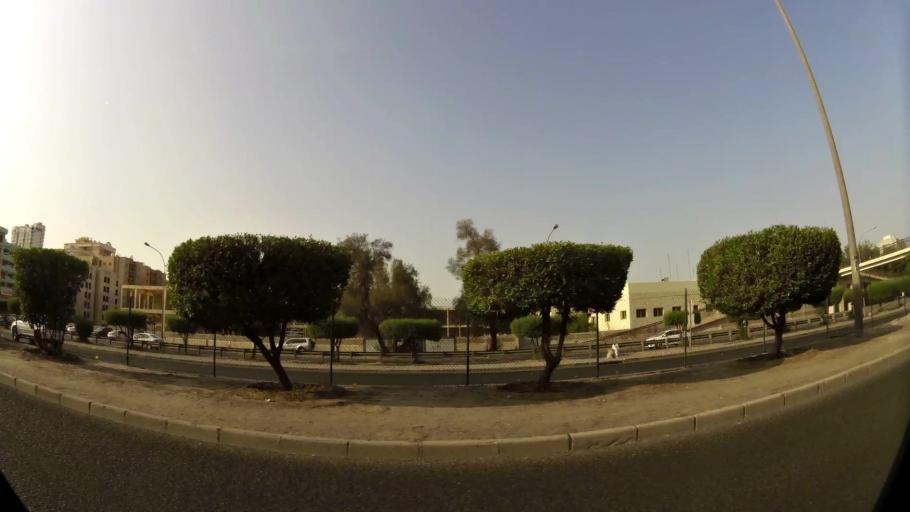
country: KW
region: Muhafazat Hawalli
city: Hawalli
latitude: 29.3300
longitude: 48.0338
